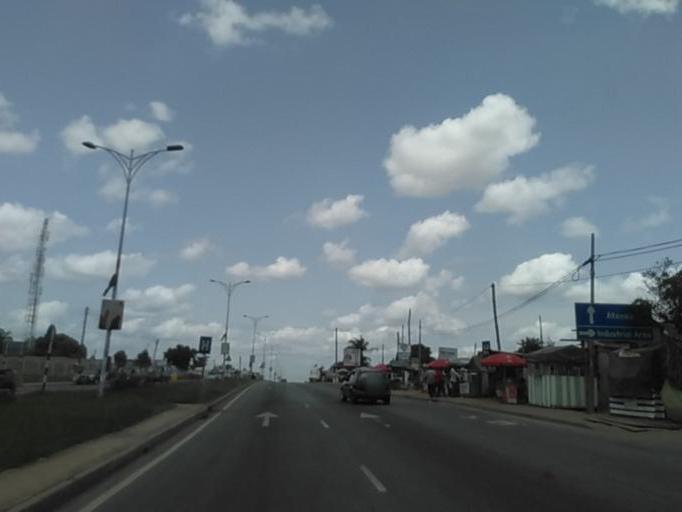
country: GH
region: Ashanti
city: Kumasi
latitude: 6.6674
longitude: -1.6056
